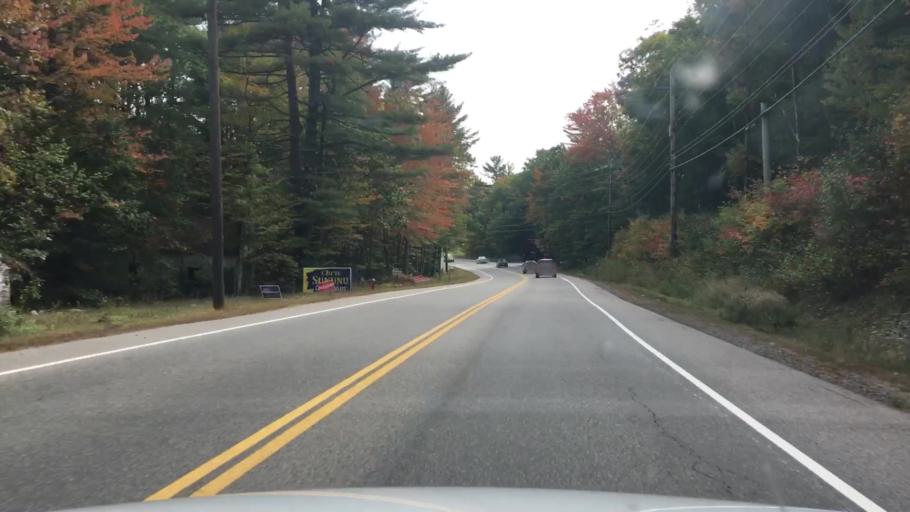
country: US
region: New Hampshire
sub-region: Carroll County
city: North Conway
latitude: 44.1099
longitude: -71.1649
